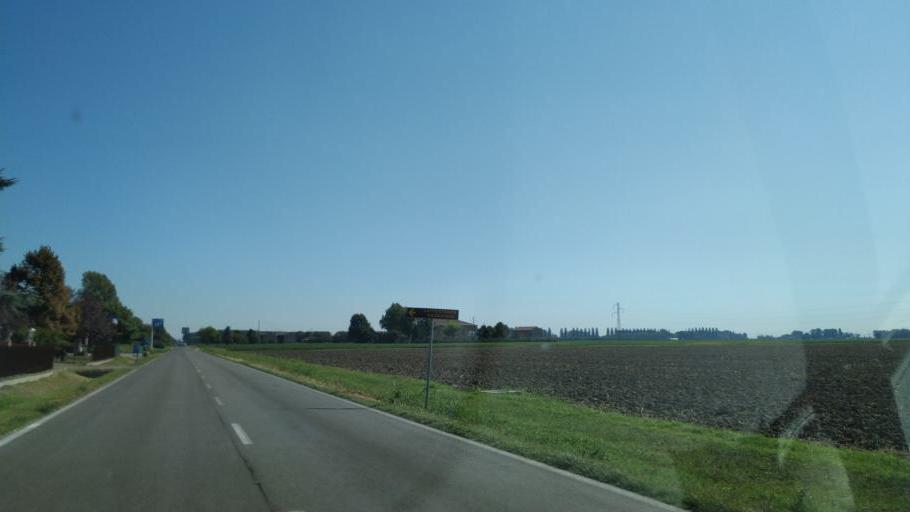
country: IT
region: Emilia-Romagna
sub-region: Provincia di Ferrara
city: San Carlo
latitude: 44.8085
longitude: 11.4298
